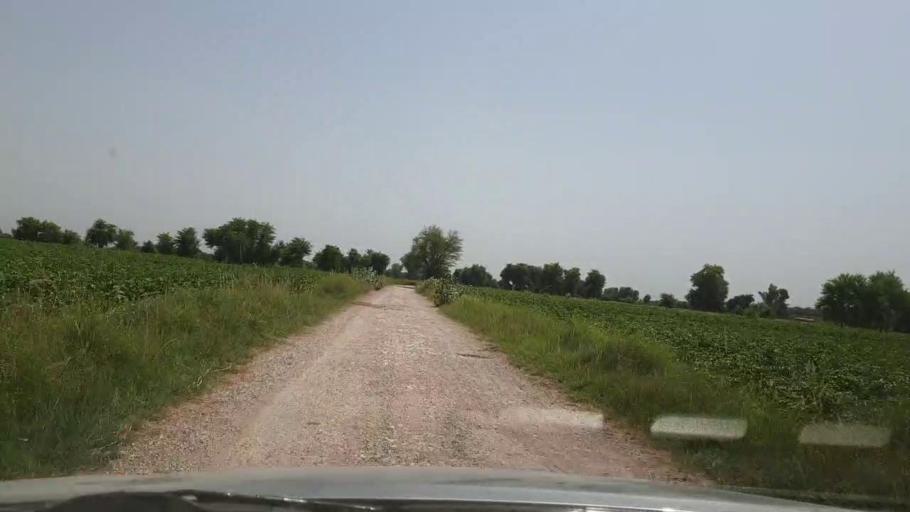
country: PK
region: Sindh
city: Pano Aqil
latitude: 27.7955
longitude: 69.2430
